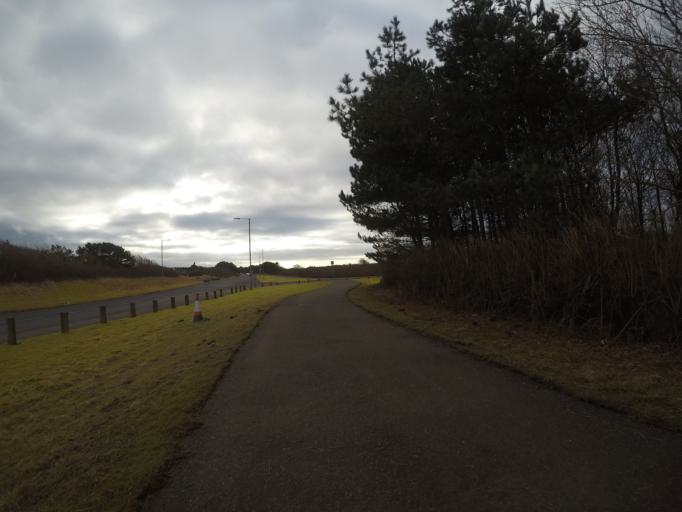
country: GB
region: Scotland
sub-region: North Ayrshire
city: Irvine
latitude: 55.6005
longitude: -4.6795
